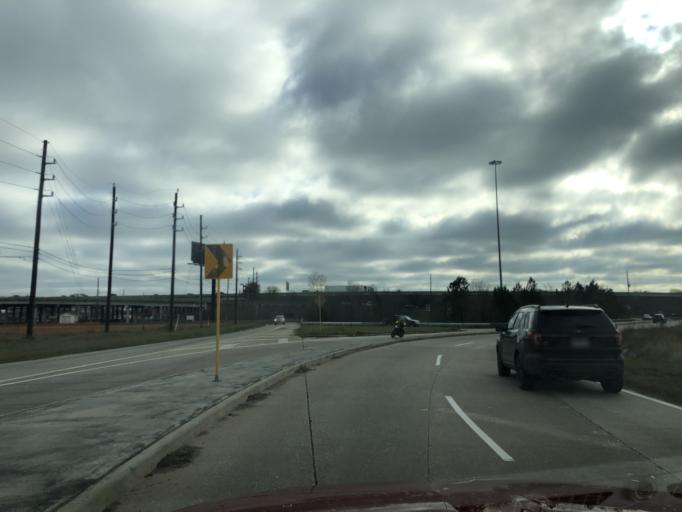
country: US
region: Texas
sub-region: Harris County
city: Spring
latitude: 30.0830
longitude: -95.4393
